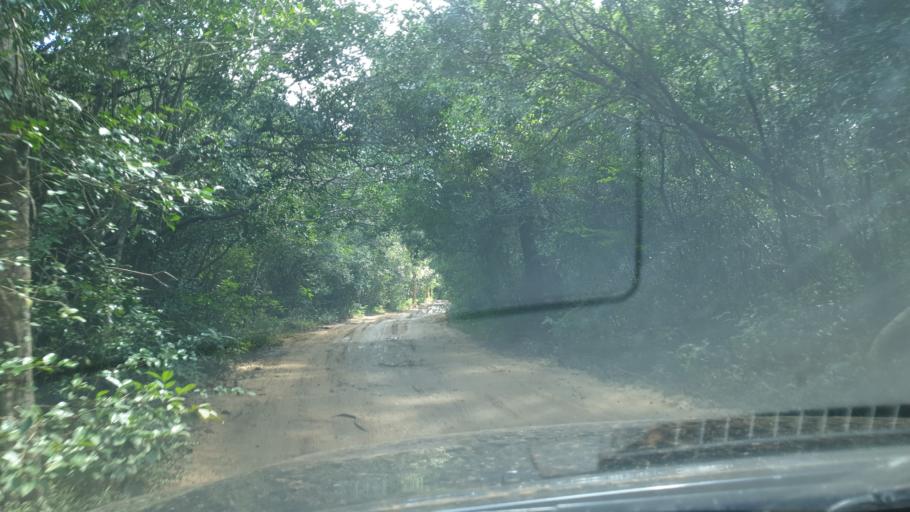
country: LK
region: North Central
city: Anuradhapura
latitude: 8.4194
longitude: 80.0241
